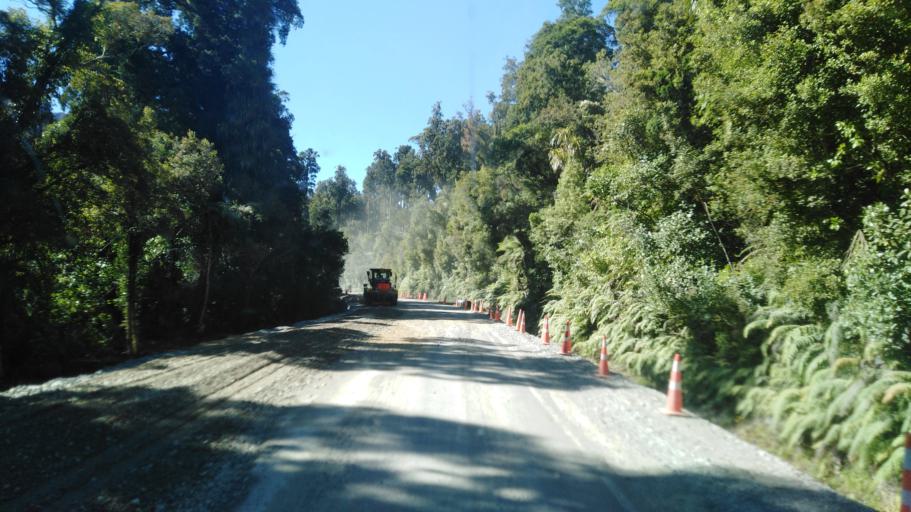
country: NZ
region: West Coast
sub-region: Buller District
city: Westport
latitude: -41.5282
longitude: 172.0035
